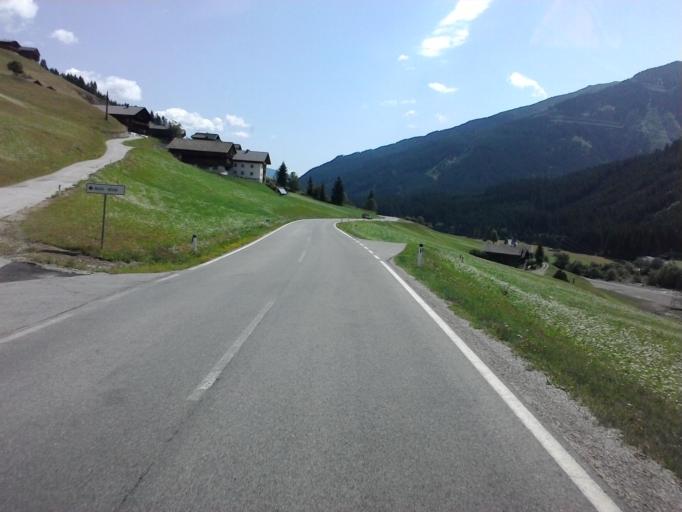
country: AT
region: Tyrol
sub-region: Politischer Bezirk Lienz
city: Obertilliach
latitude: 46.7013
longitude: 12.6538
